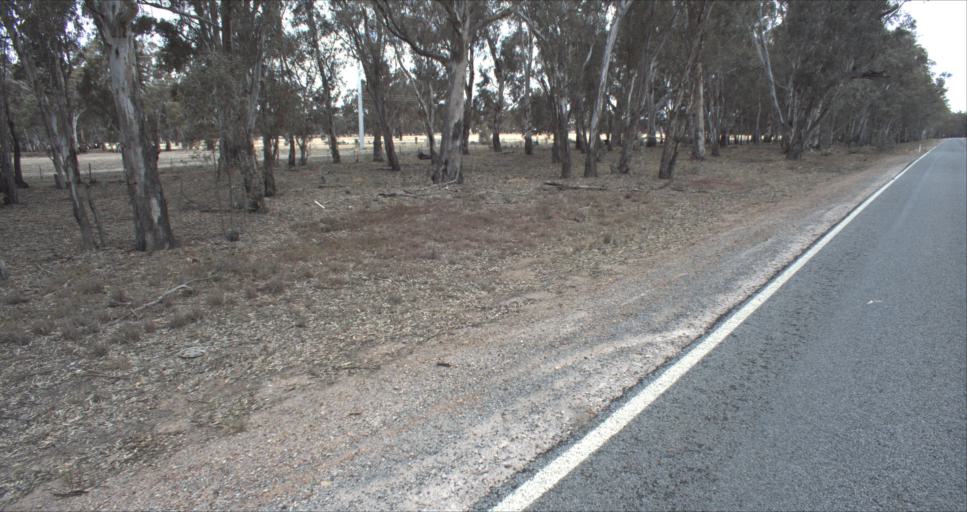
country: AU
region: New South Wales
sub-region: Leeton
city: Leeton
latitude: -34.6257
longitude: 146.3795
